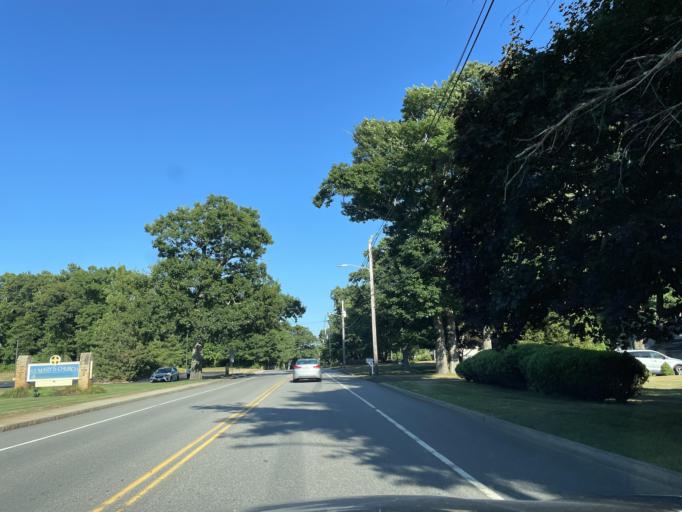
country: US
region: Massachusetts
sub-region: Bristol County
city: Mansfield
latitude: 42.0339
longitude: -71.2033
